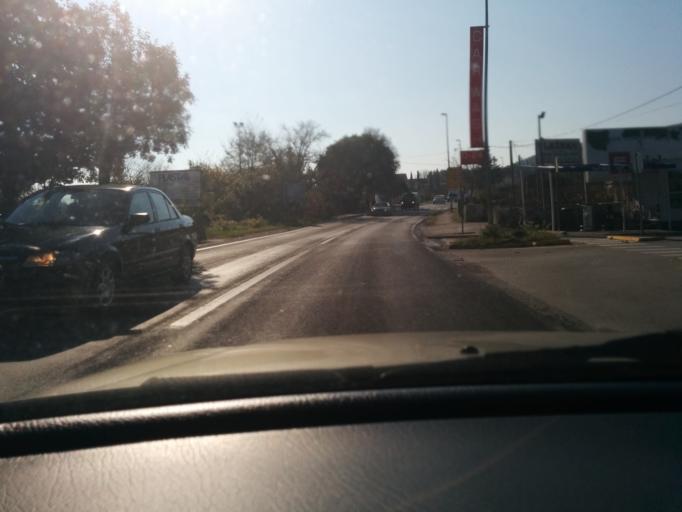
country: HR
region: Splitsko-Dalmatinska
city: Brnaze
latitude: 43.6824
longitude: 16.6501
